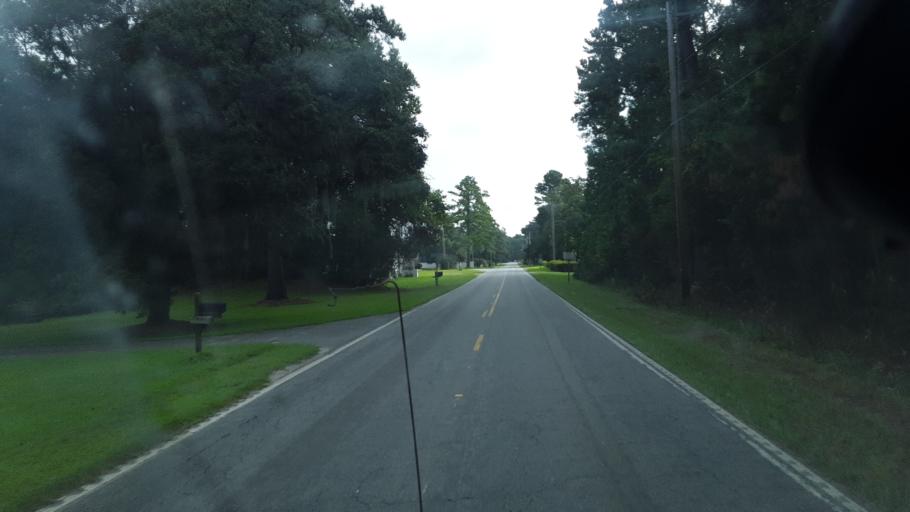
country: US
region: South Carolina
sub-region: Horry County
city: Conway
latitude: 33.8195
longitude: -79.0870
